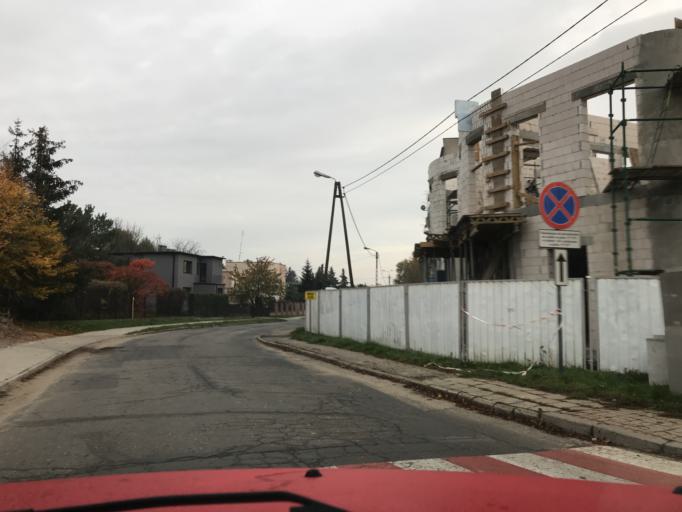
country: PL
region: Greater Poland Voivodeship
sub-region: Kalisz
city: Kalisz
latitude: 51.7538
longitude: 18.0672
